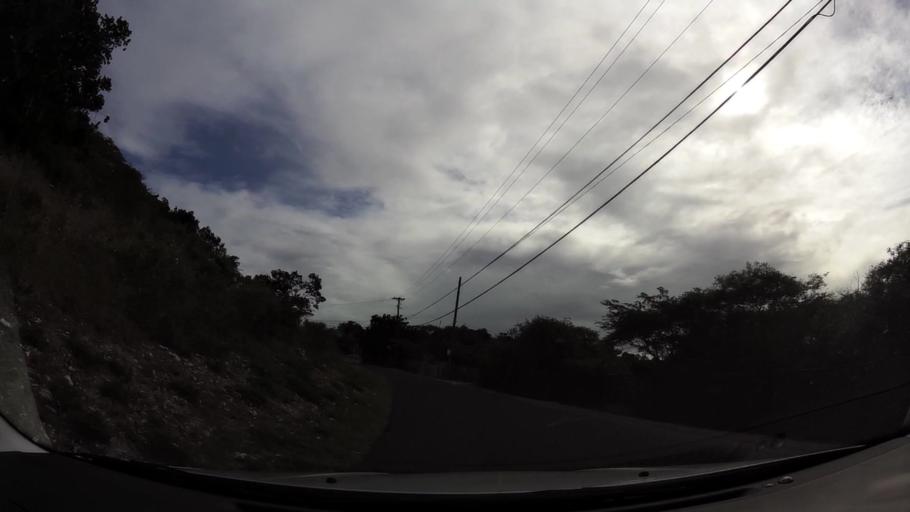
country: AG
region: Saint Peter
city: Parham
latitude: 17.0917
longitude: -61.6929
